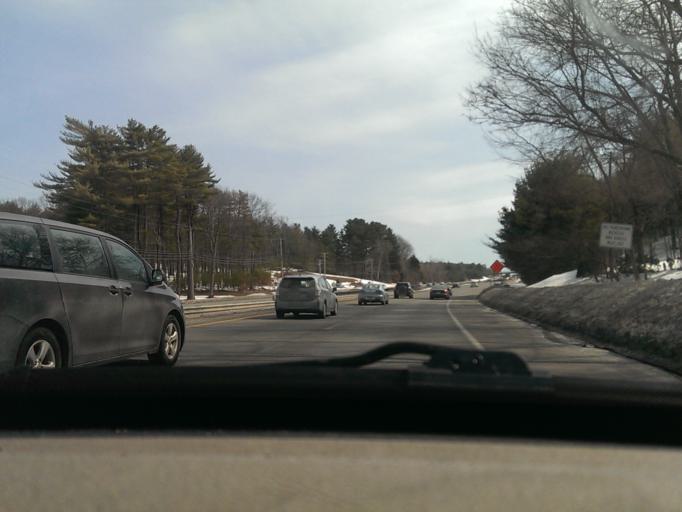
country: US
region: Massachusetts
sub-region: Worcester County
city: Sutton
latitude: 42.1567
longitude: -71.7302
